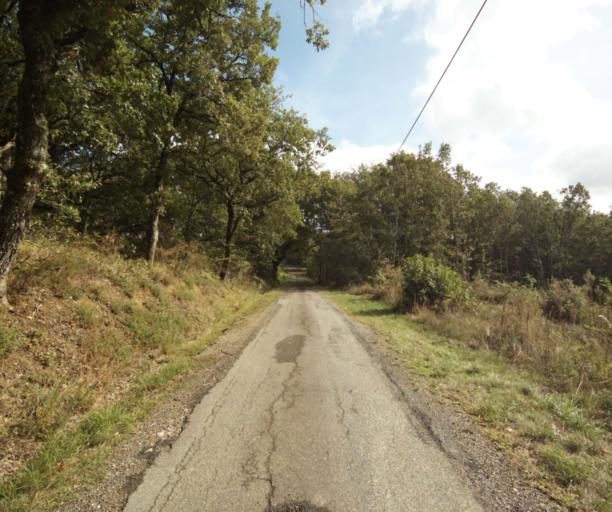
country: FR
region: Midi-Pyrenees
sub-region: Departement du Tarn-et-Garonne
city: Beaumont-de-Lomagne
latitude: 43.8624
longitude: 1.0880
